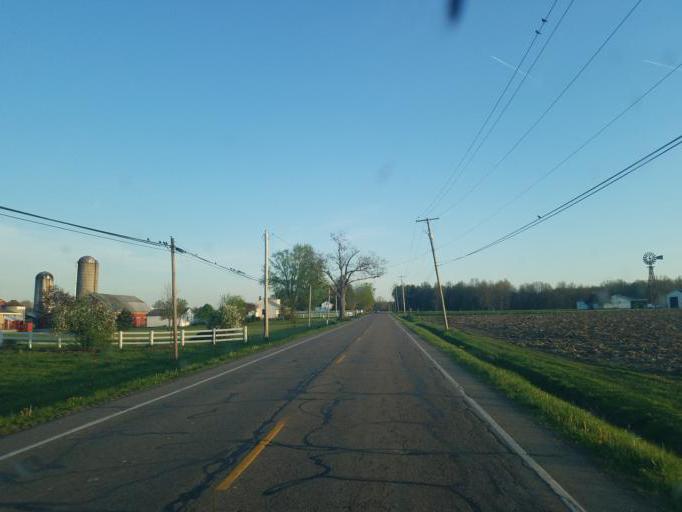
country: US
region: Ohio
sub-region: Trumbull County
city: Cortland
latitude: 41.4351
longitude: -80.5889
